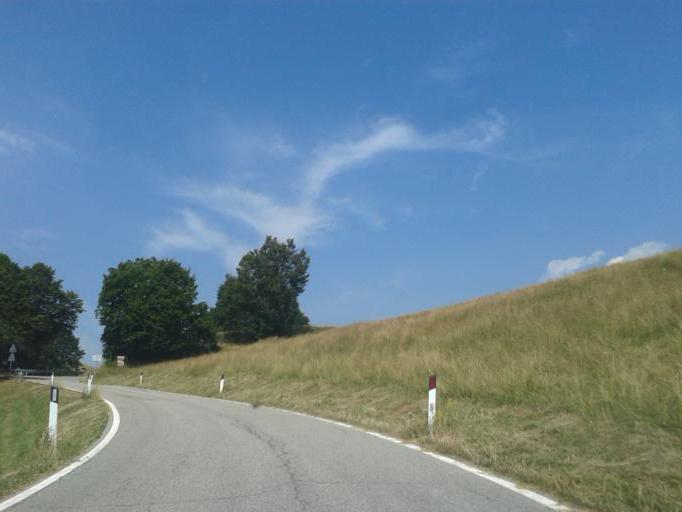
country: IT
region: Trentino-Alto Adige
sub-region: Provincia di Trento
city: Avio
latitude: 45.7779
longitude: 10.9084
